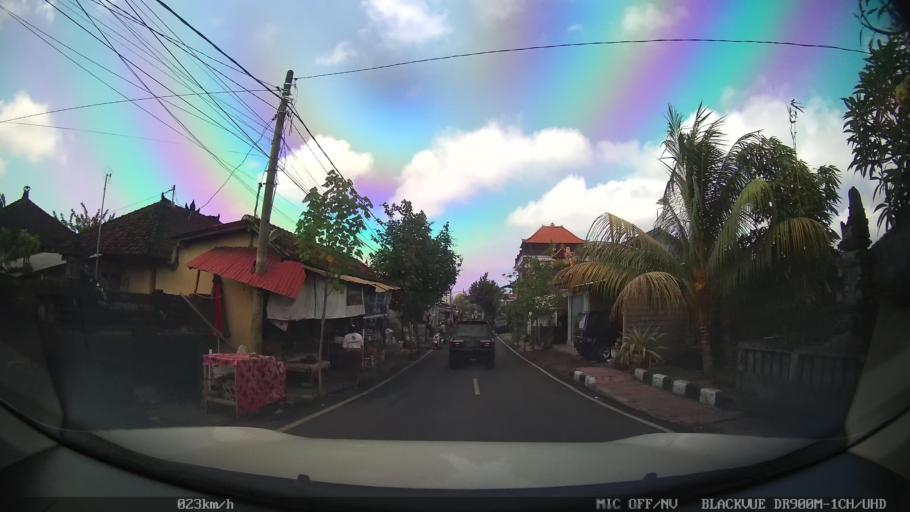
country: ID
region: Bali
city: Banjar Pasekan
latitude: -8.5973
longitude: 115.2853
